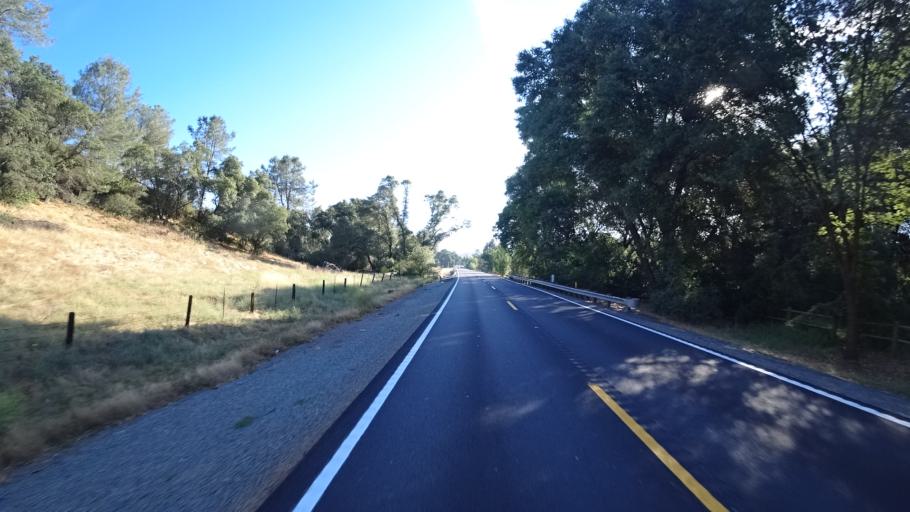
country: US
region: California
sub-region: Calaveras County
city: Valley Springs
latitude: 38.2011
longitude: -120.7958
